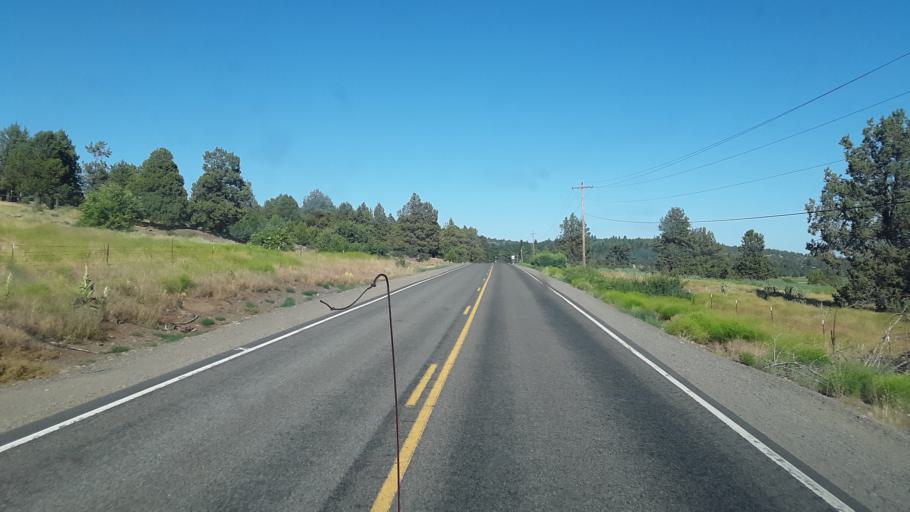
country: US
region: Oregon
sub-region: Klamath County
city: Klamath Falls
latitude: 42.2755
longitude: -121.9006
